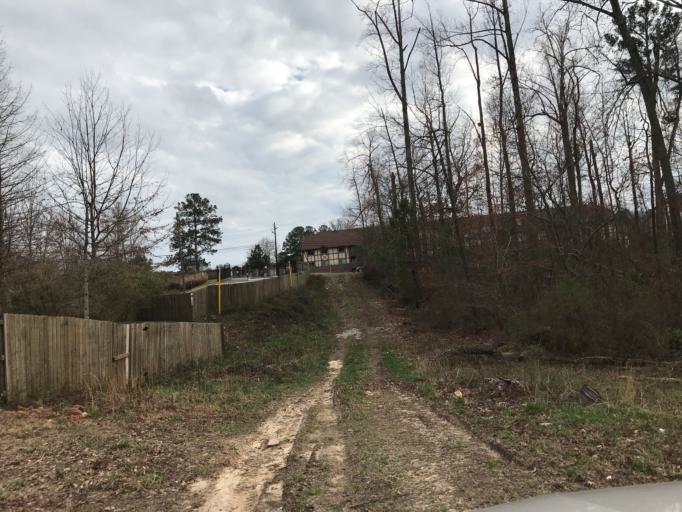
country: US
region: Georgia
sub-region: Fulton County
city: College Park
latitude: 33.6051
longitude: -84.4758
